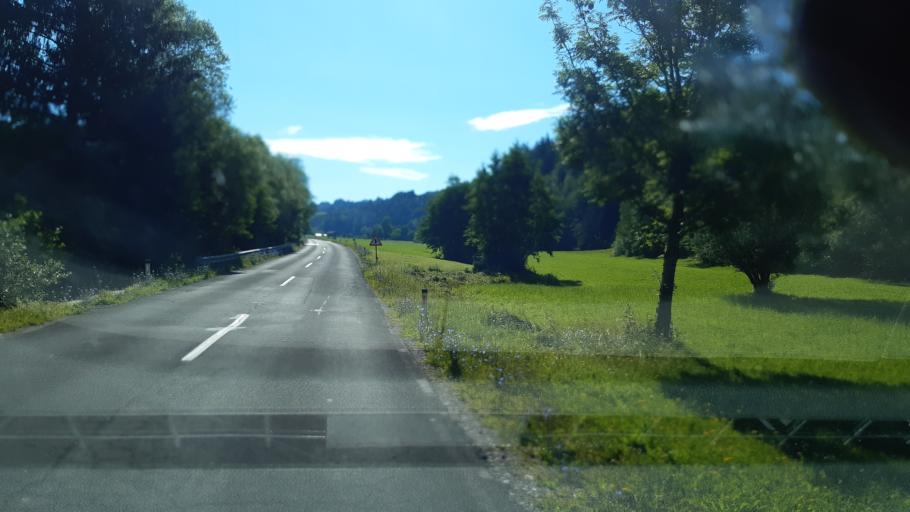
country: SI
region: Lukovica
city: Lukovica pri Domzalah
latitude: 46.2185
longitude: 14.7445
